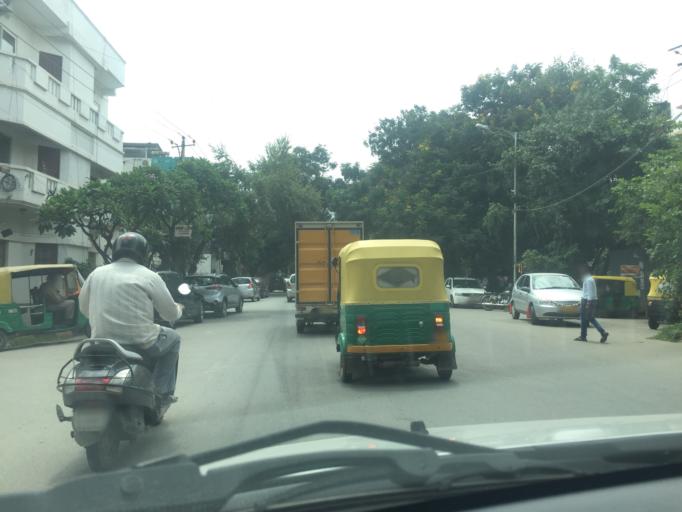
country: IN
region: Karnataka
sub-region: Bangalore Urban
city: Bangalore
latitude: 12.9635
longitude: 77.6411
